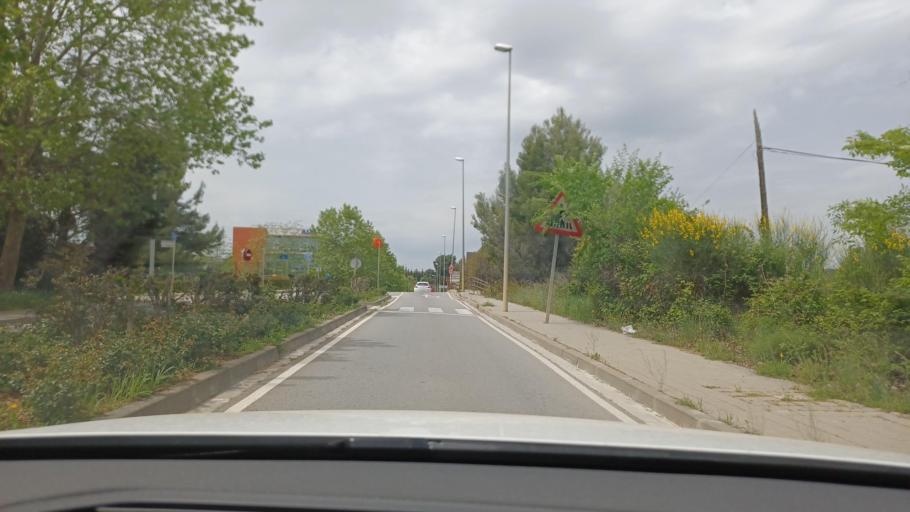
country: ES
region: Catalonia
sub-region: Provincia de Barcelona
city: Sant Cugat del Valles
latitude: 41.4843
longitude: 2.0891
